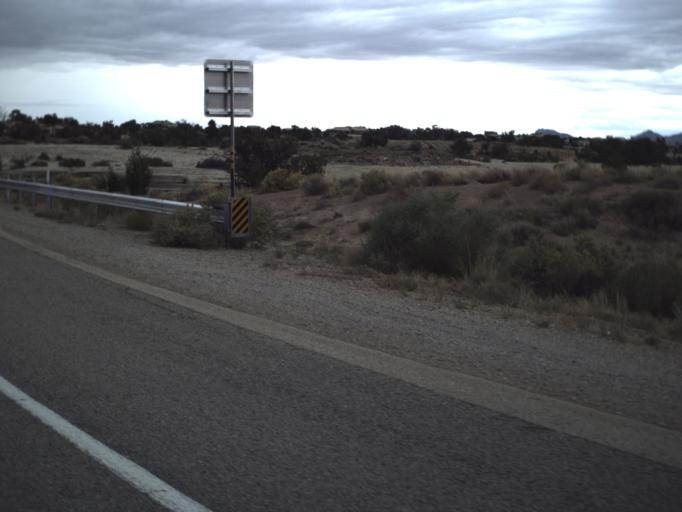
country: US
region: Utah
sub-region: Emery County
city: Ferron
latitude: 38.8299
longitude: -111.1200
